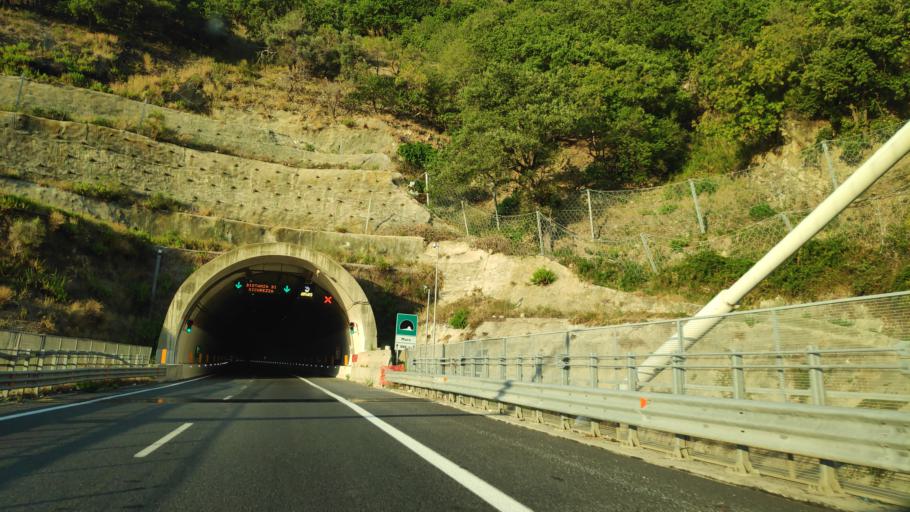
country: IT
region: Calabria
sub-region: Provincia di Reggio Calabria
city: Bagnara Calabra
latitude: 38.2555
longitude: 15.7699
